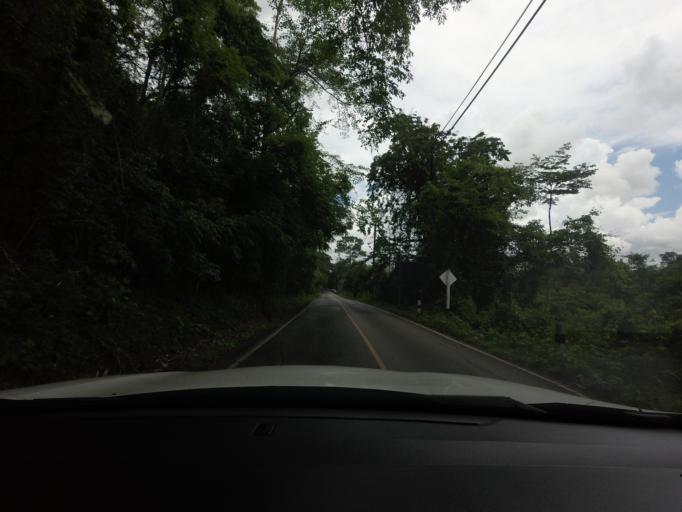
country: TH
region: Nakhon Ratchasima
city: Pak Chong
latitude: 14.5050
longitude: 101.3808
